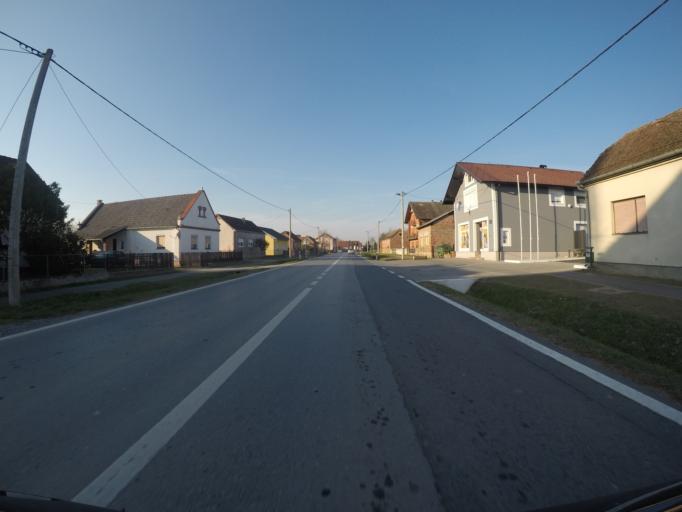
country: HU
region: Somogy
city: Barcs
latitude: 45.9066
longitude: 17.4414
